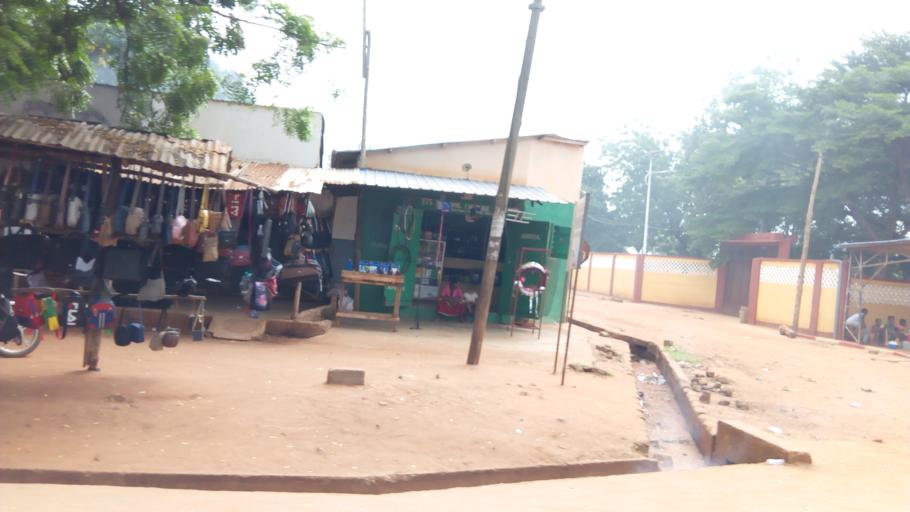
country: TG
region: Maritime
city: Tsevie
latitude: 6.4307
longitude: 1.2127
